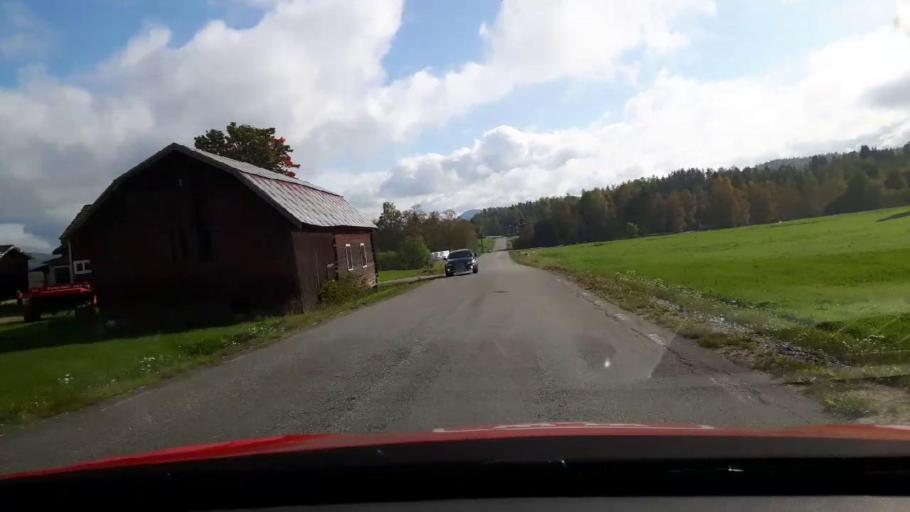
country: SE
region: Gaevleborg
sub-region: Ljusdals Kommun
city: Jaervsoe
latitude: 61.7542
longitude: 16.1292
